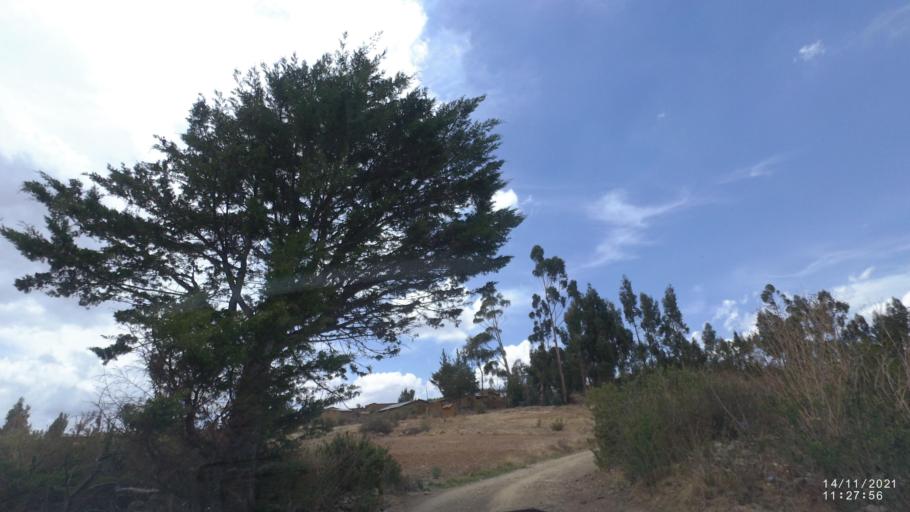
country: BO
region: Cochabamba
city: Colomi
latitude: -17.3420
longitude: -66.0133
